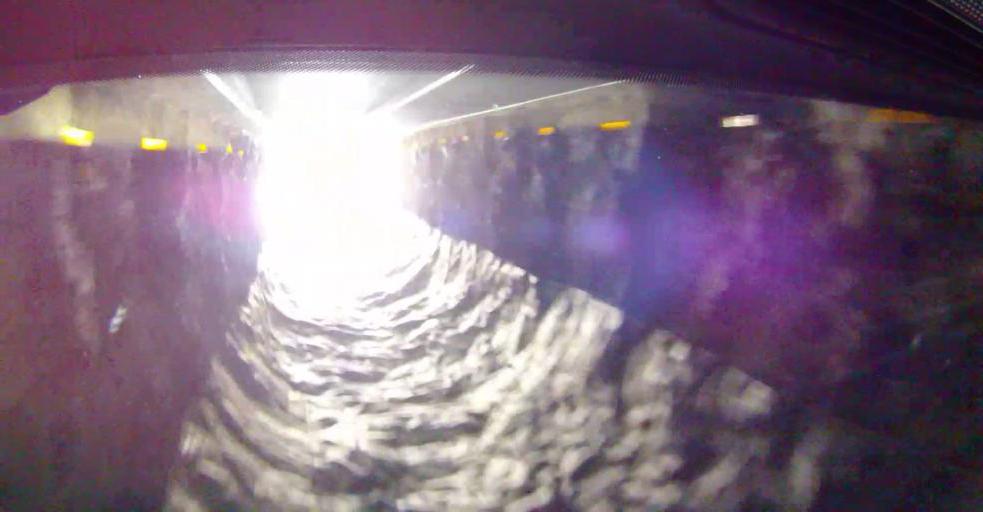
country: ES
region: Castille and Leon
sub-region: Provincia de Leon
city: Puebla de Lillo
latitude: 42.9336
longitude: -5.2822
